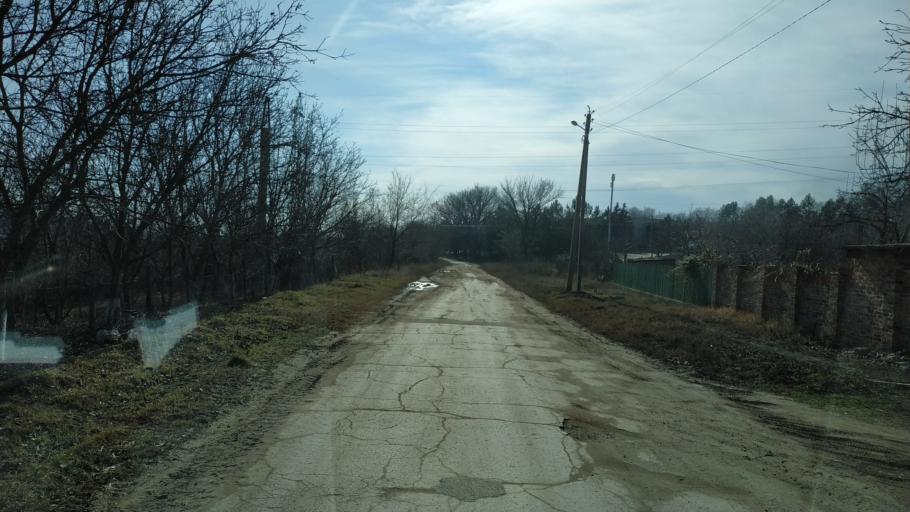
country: MD
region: Nisporeni
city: Nisporeni
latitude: 47.0616
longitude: 28.1714
